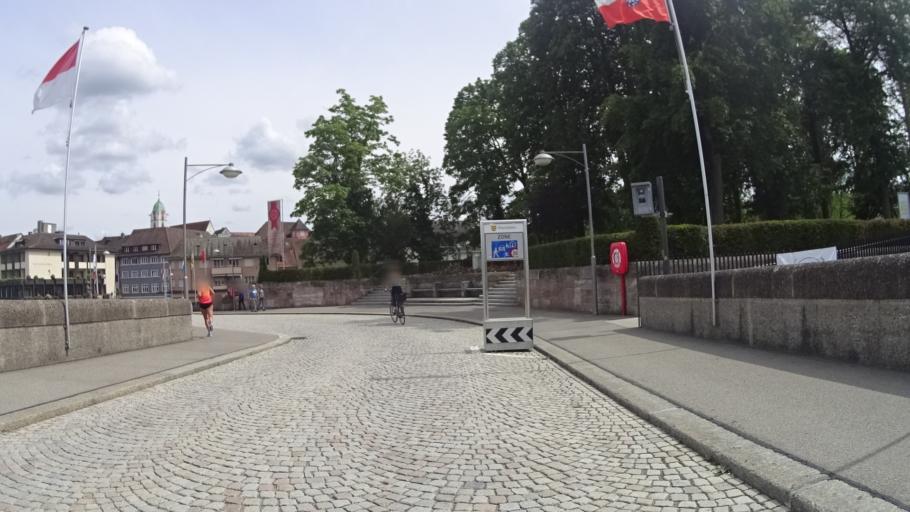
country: CH
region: Aargau
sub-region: Bezirk Rheinfelden
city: Rheinfelden
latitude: 47.5552
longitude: 7.7896
